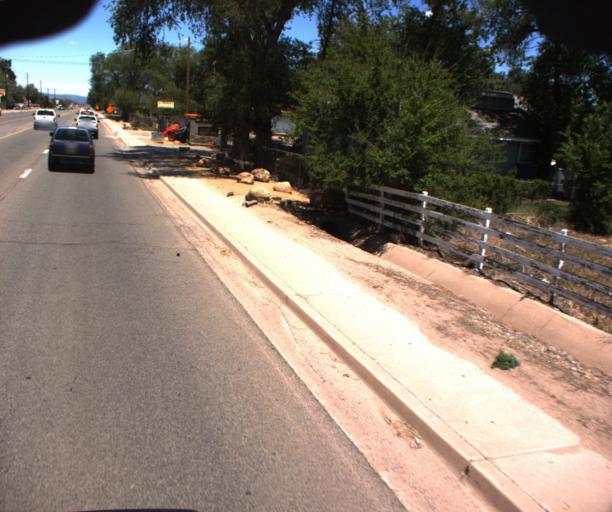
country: US
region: Arizona
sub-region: Yavapai County
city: Chino Valley
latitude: 34.7624
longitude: -112.4535
